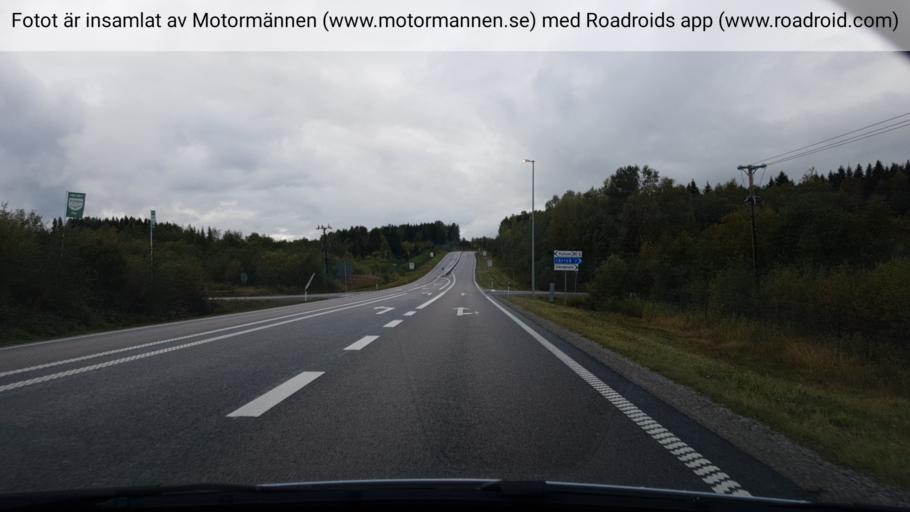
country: SE
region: Vaesternorrland
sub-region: OErnskoeldsviks Kommun
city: Ornskoldsvik
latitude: 63.3115
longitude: 18.9358
